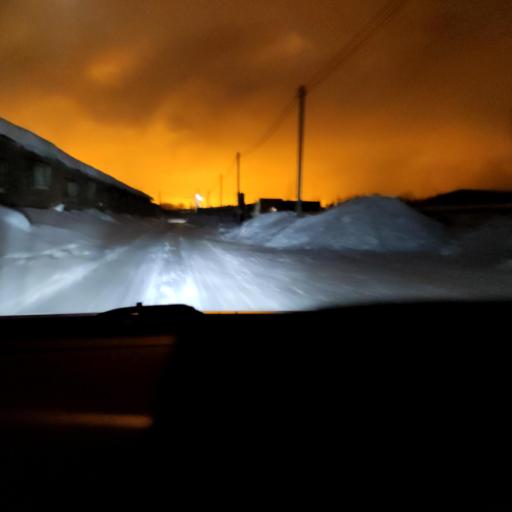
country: RU
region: Tatarstan
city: Osinovo
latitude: 55.8759
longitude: 48.9540
